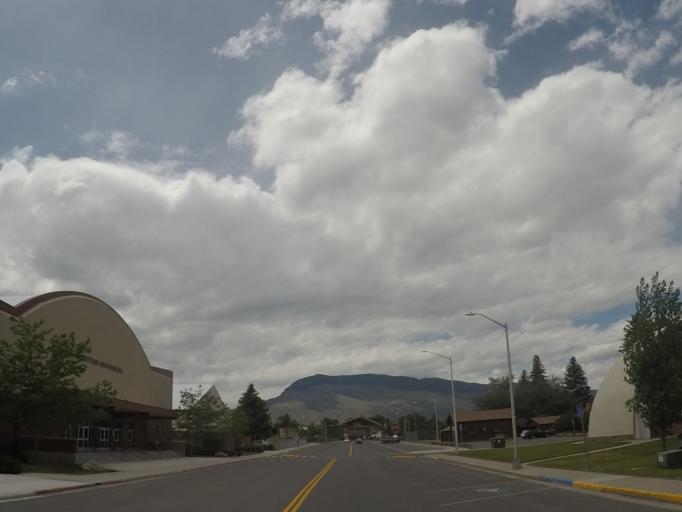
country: US
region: Wyoming
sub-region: Park County
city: Cody
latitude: 44.5250
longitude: -109.0689
